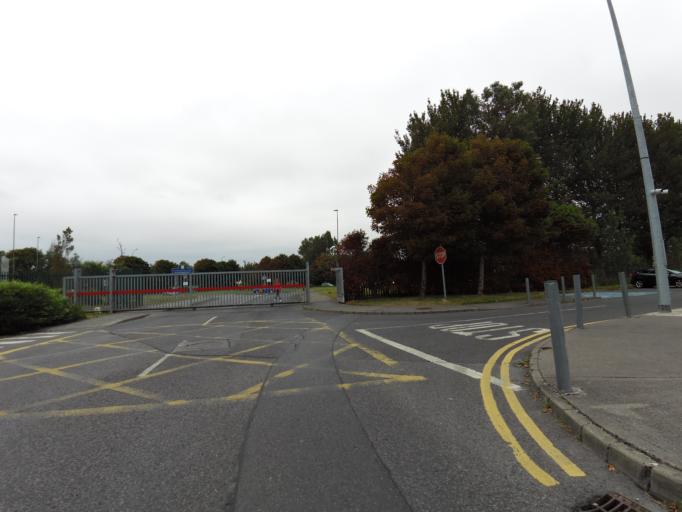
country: IE
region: Connaught
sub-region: County Galway
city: Gaillimh
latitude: 53.2785
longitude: -9.0689
